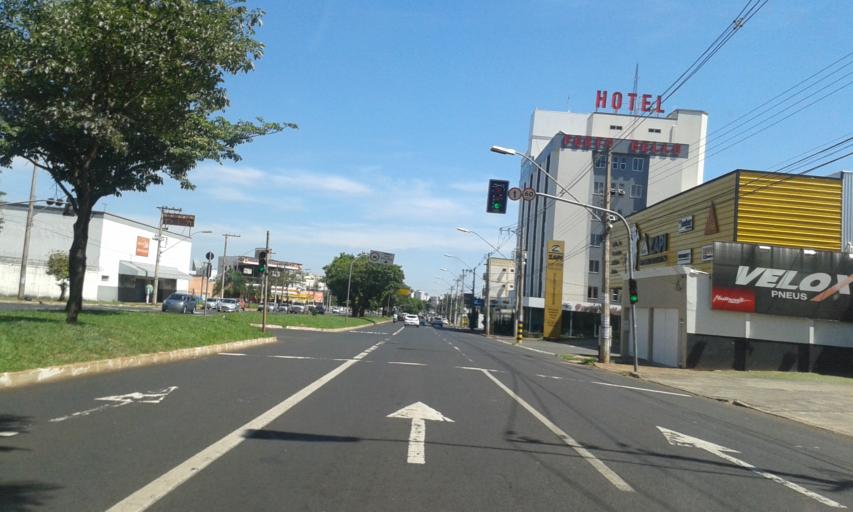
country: BR
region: Minas Gerais
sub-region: Uberlandia
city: Uberlandia
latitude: -18.9270
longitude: -48.2555
